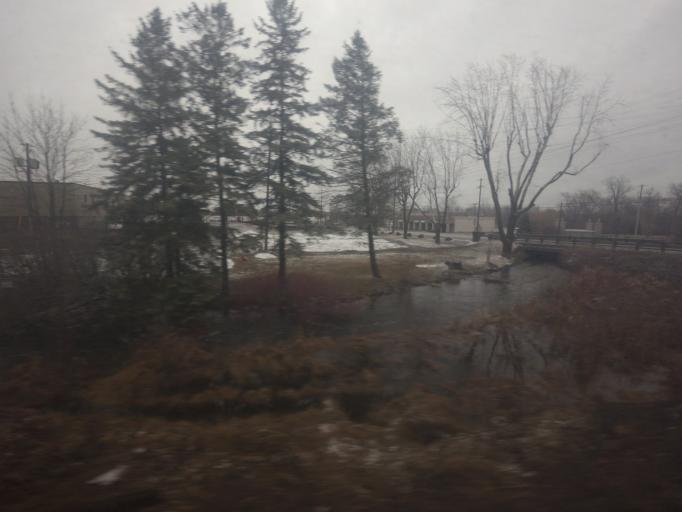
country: CA
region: Ontario
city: Brockville
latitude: 44.6083
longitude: -75.6943
